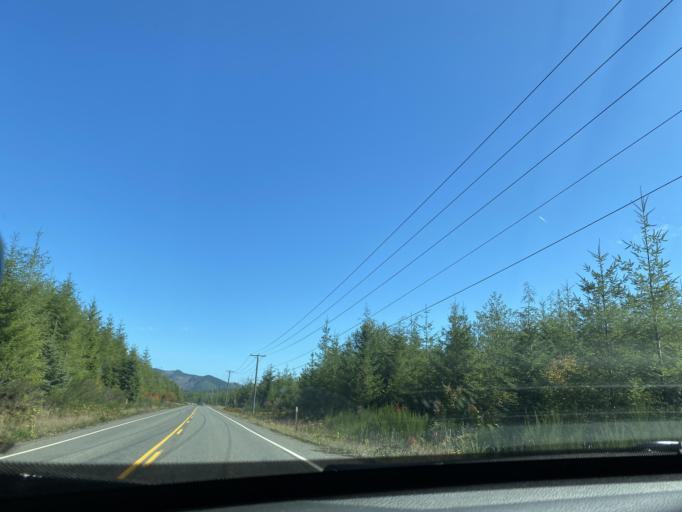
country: US
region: Washington
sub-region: Clallam County
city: Forks
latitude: 47.9626
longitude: -124.4257
